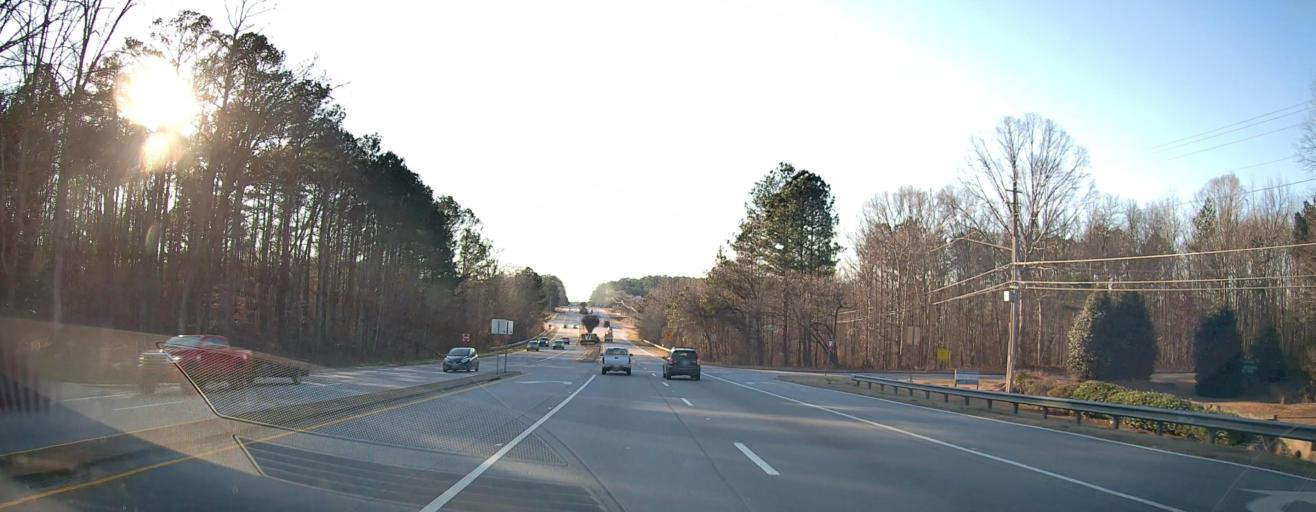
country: US
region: Georgia
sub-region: Fayette County
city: Fayetteville
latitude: 33.4481
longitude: -84.4785
